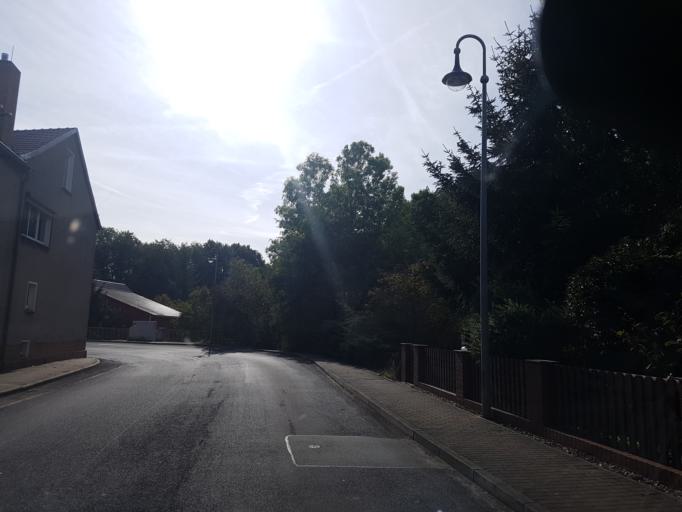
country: DE
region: Brandenburg
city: Schlieben
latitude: 51.7035
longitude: 13.4122
